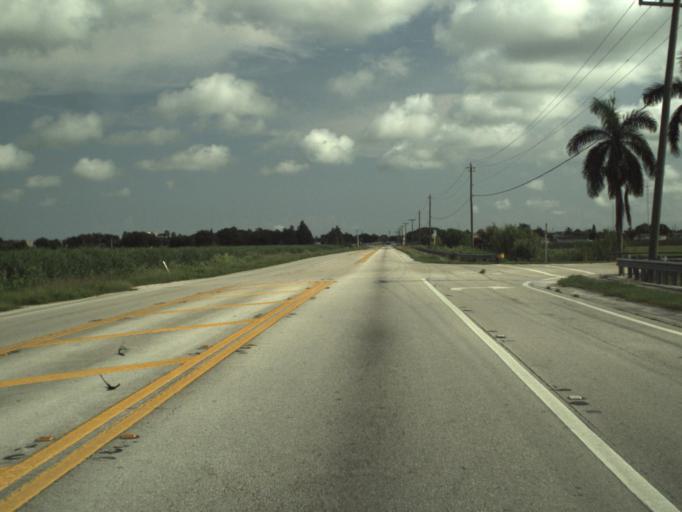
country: US
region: Florida
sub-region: Palm Beach County
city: Belle Glade Camp
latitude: 26.6708
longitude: -80.6868
